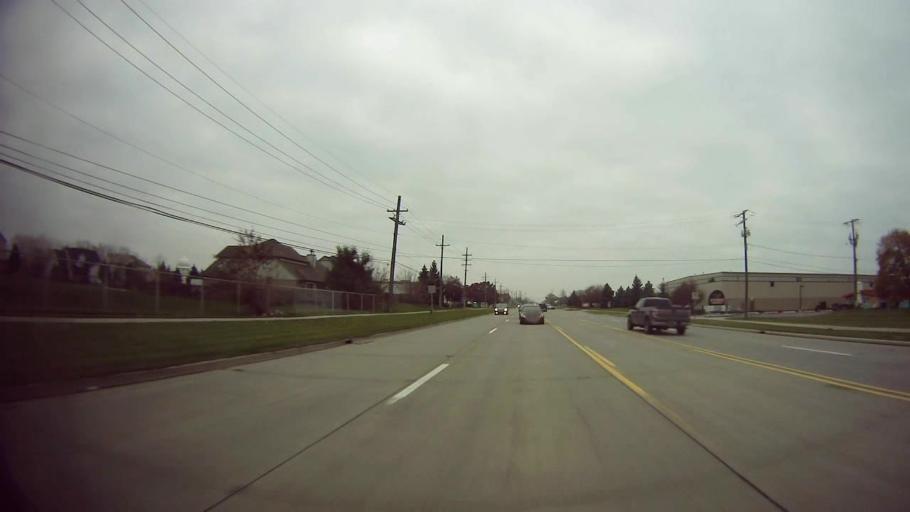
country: US
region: Michigan
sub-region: Oakland County
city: Madison Heights
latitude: 42.5388
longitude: -83.0871
